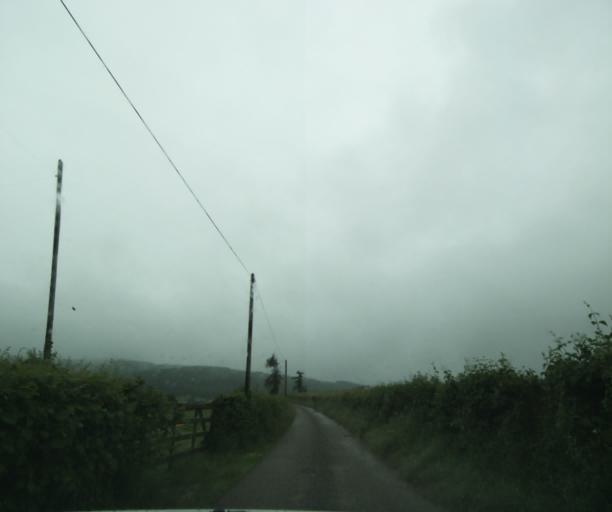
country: FR
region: Bourgogne
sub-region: Departement de Saone-et-Loire
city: La Clayette
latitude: 46.3677
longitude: 4.3800
